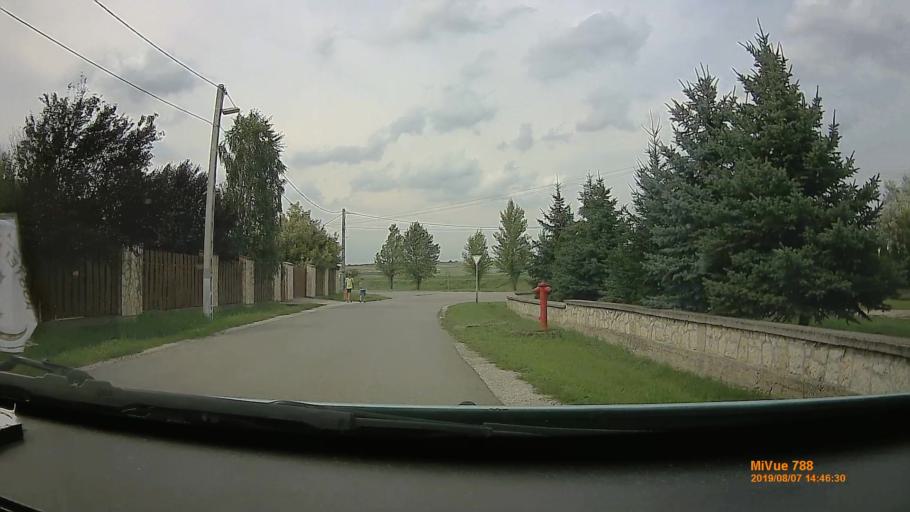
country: HU
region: Borsod-Abauj-Zemplen
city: Halmaj
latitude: 48.2481
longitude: 20.9909
